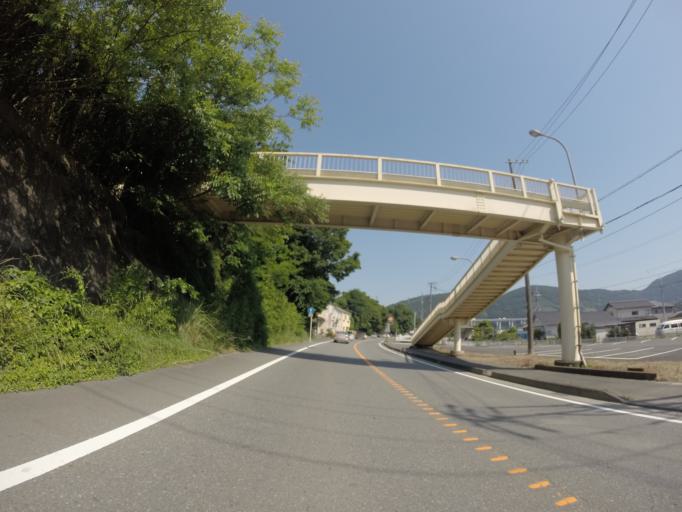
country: JP
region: Shizuoka
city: Fujinomiya
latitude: 35.1870
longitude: 138.6000
